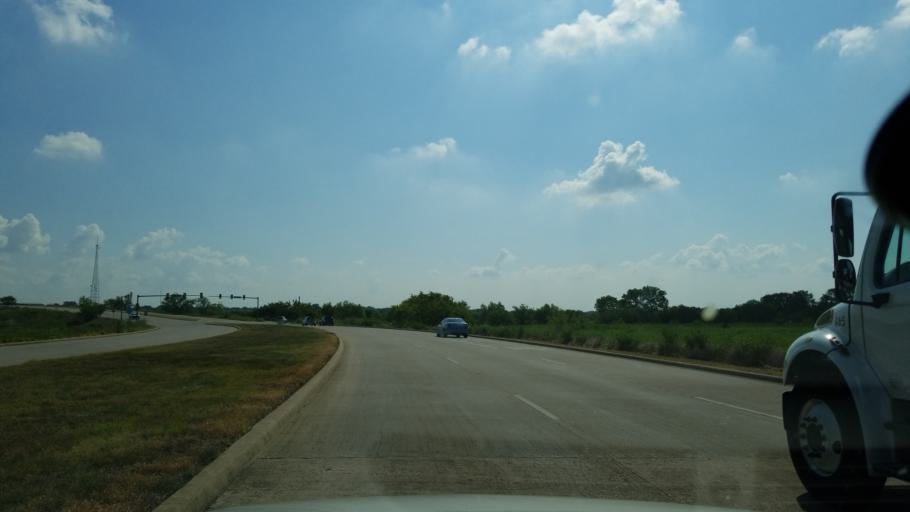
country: US
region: Texas
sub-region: Tarrant County
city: Hurst
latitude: 32.8009
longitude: -97.1454
